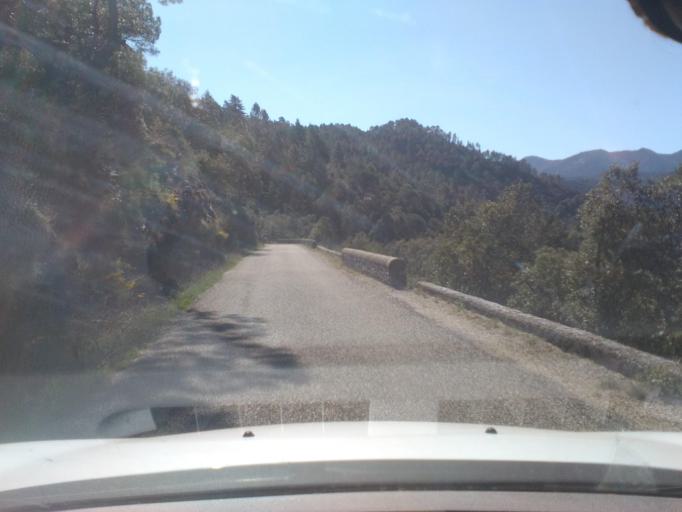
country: FR
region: Languedoc-Roussillon
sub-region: Departement du Gard
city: Lasalle
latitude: 44.1296
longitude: 3.7622
